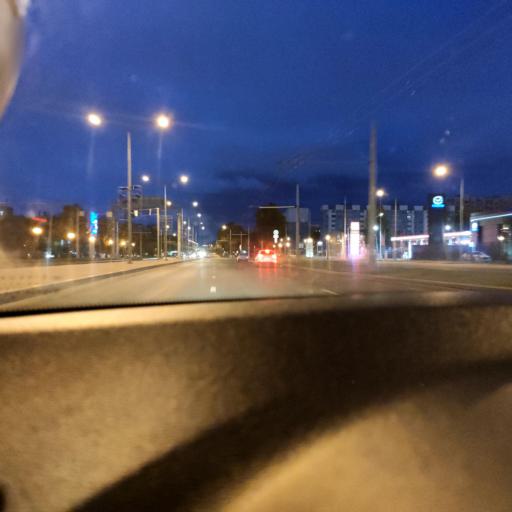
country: RU
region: Samara
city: Samara
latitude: 53.2492
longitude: 50.2194
